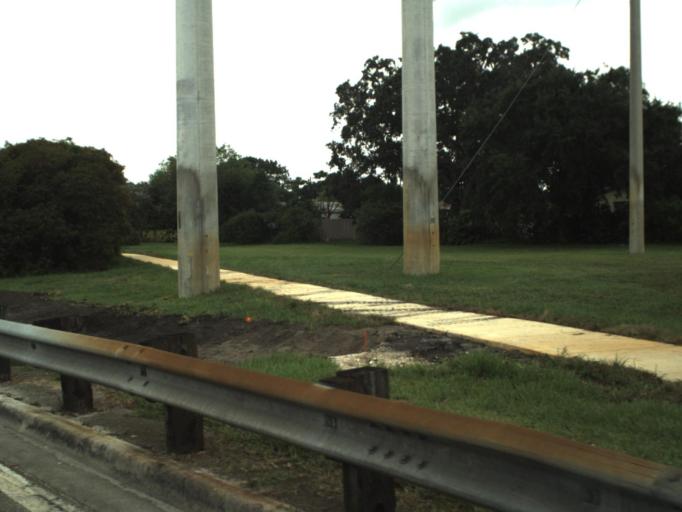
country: US
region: Florida
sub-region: Broward County
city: Pembroke Pines
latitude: 26.0316
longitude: -80.2244
